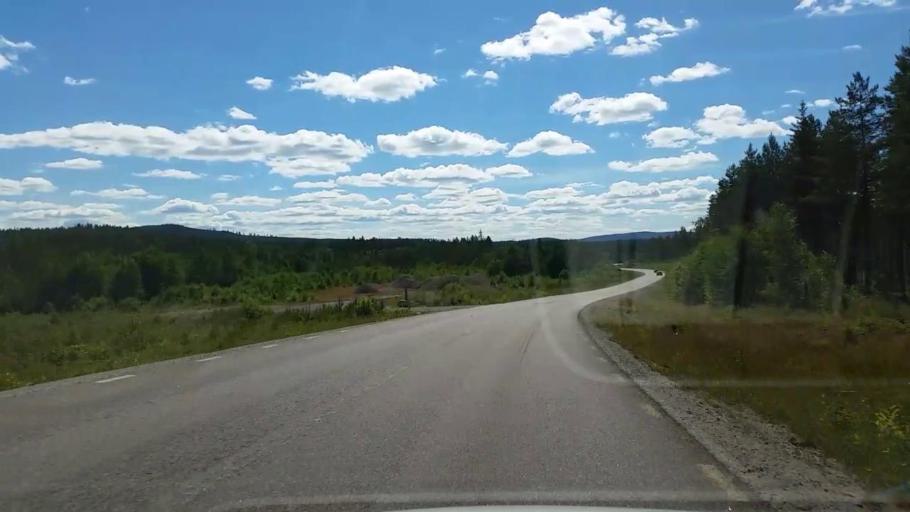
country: SE
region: Dalarna
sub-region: Faluns Kommun
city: Svardsjo
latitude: 61.0149
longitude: 15.7542
